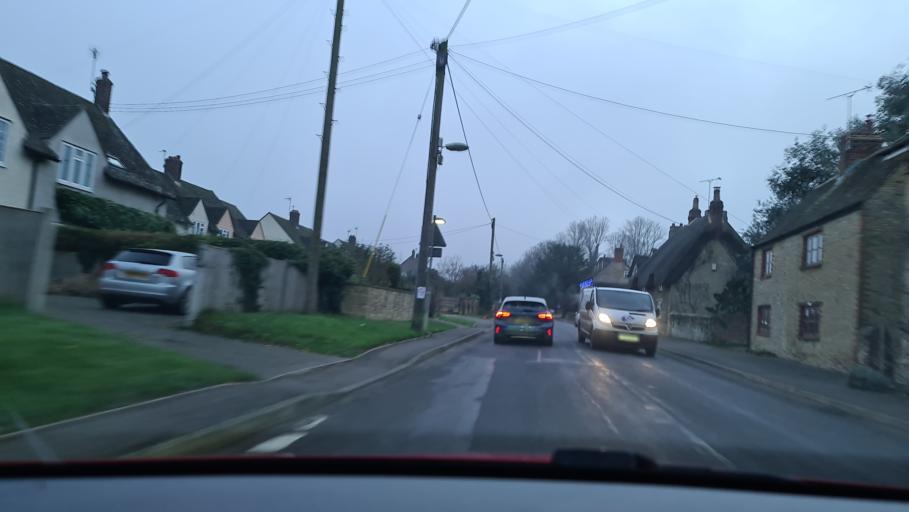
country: GB
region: England
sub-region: Oxfordshire
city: Bicester
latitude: 51.8915
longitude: -1.1904
